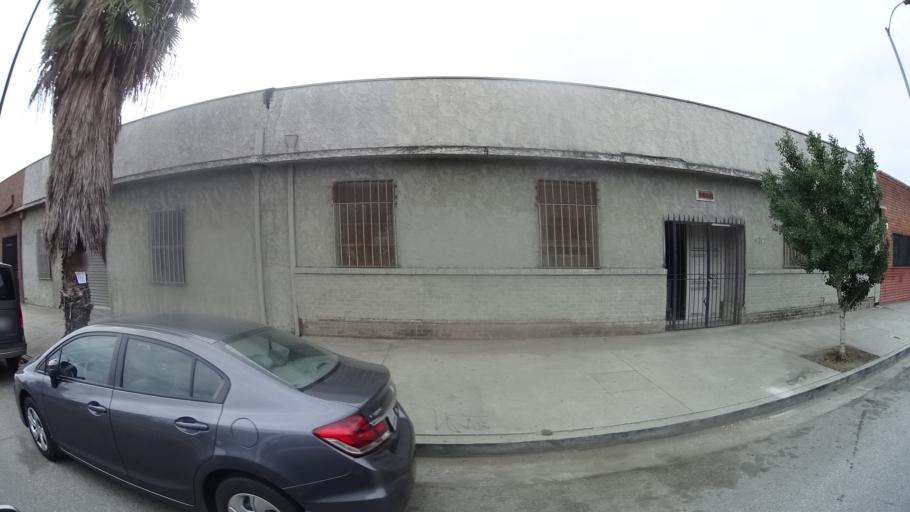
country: US
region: California
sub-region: Los Angeles County
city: View Park-Windsor Hills
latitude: 34.0255
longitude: -118.3423
